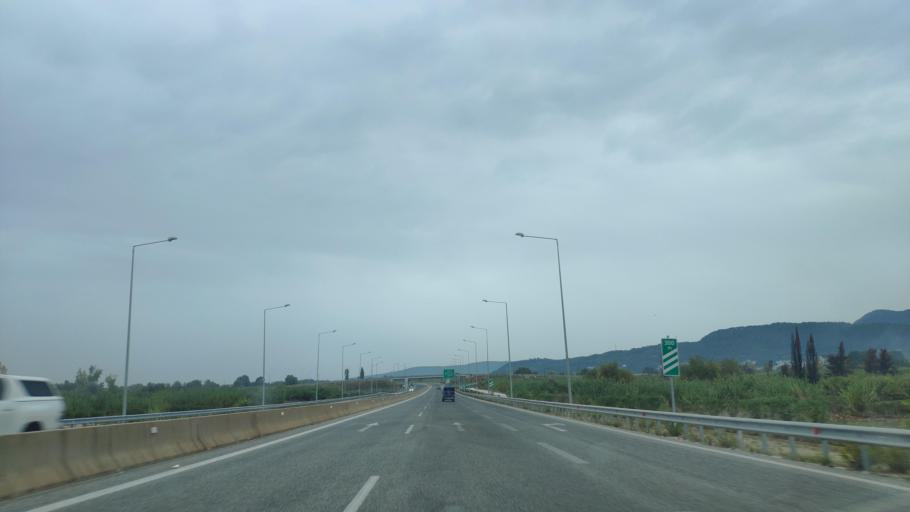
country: GR
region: Epirus
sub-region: Nomos Artas
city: Kampi
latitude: 39.2151
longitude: 20.9058
